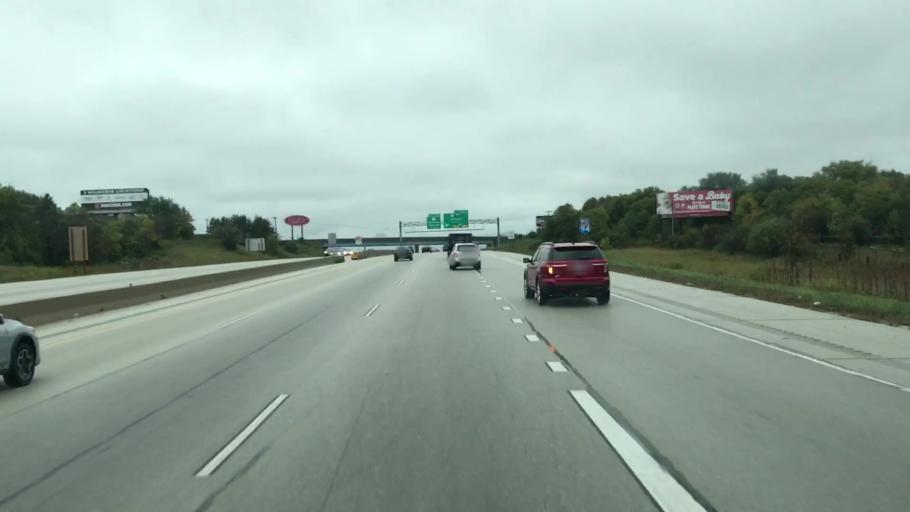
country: US
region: Wisconsin
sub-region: Waukesha County
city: Waukesha
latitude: 43.0488
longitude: -88.2327
